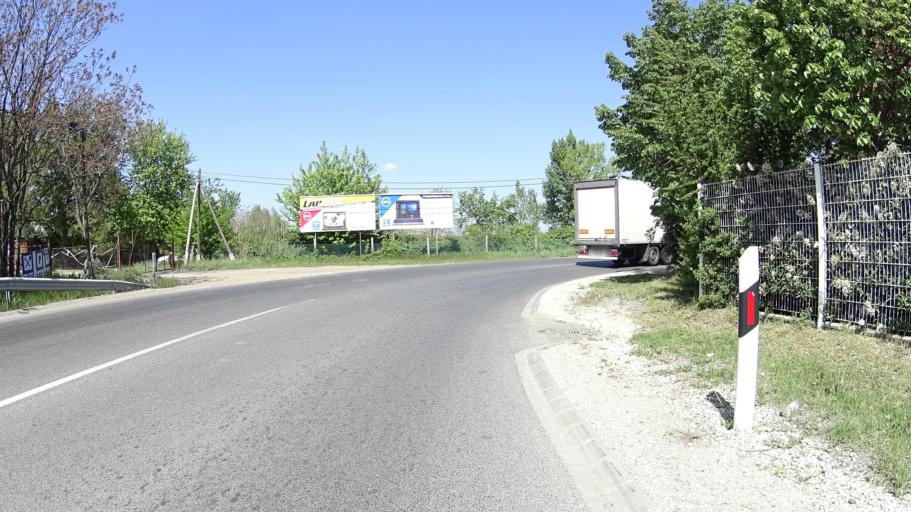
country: HU
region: Pest
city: Gyal
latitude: 47.3603
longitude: 19.2027
